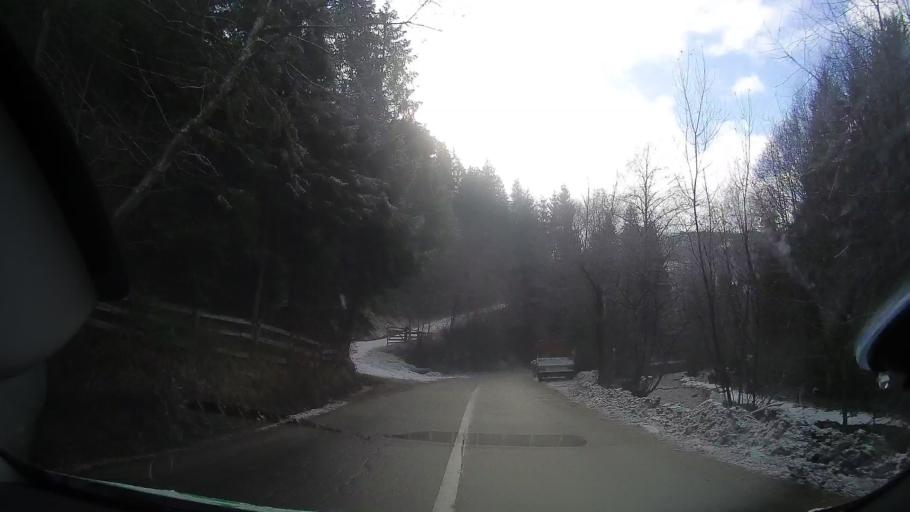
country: RO
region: Alba
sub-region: Comuna Horea
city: Horea
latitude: 46.4841
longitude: 22.9621
